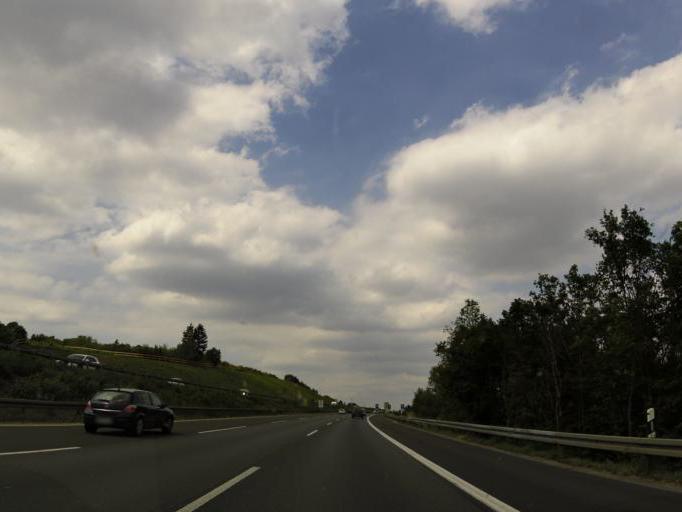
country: DE
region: Bavaria
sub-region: Regierungsbezirk Unterfranken
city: Randersacker
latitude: 49.7442
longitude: 9.9675
